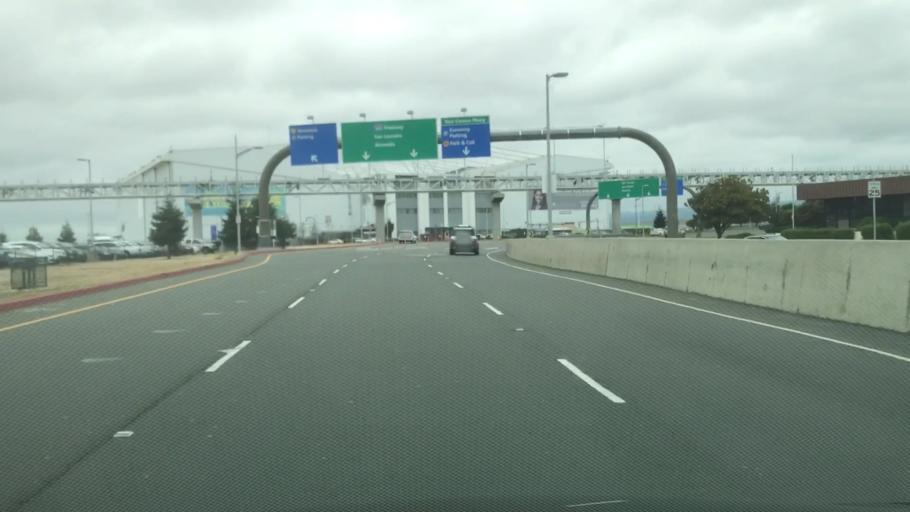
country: US
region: California
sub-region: Alameda County
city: San Leandro
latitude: 37.7149
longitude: -122.2080
